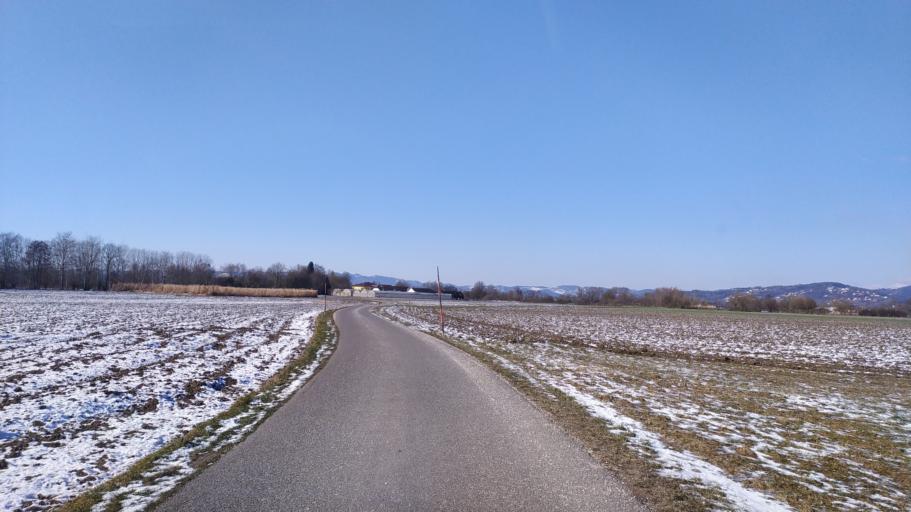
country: AT
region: Upper Austria
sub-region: Politischer Bezirk Urfahr-Umgebung
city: Goldworth
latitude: 48.3328
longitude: 14.0876
